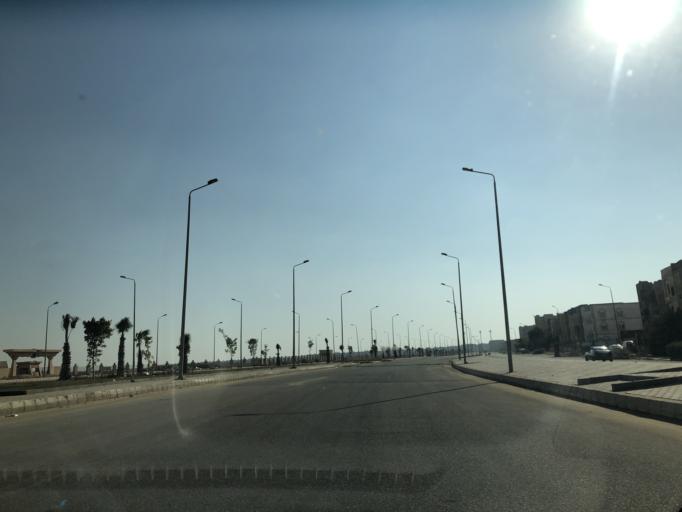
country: EG
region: Al Jizah
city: Madinat Sittah Uktubar
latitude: 29.9286
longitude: 31.0684
